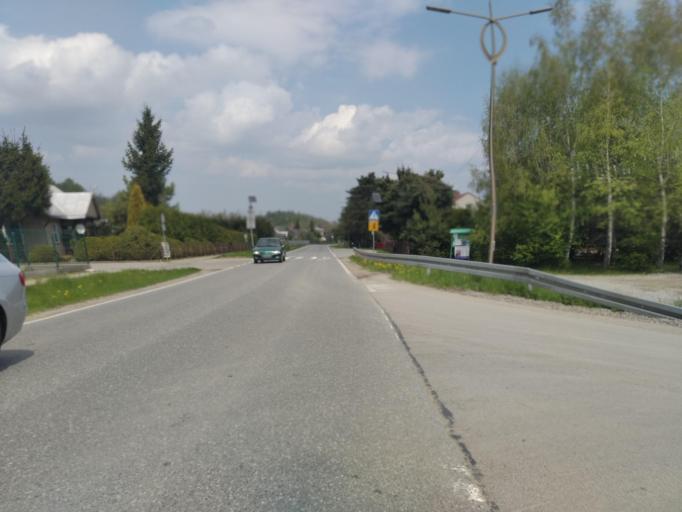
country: PL
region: Subcarpathian Voivodeship
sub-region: Powiat krosnienski
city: Rymanow
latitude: 49.5627
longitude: 21.8596
